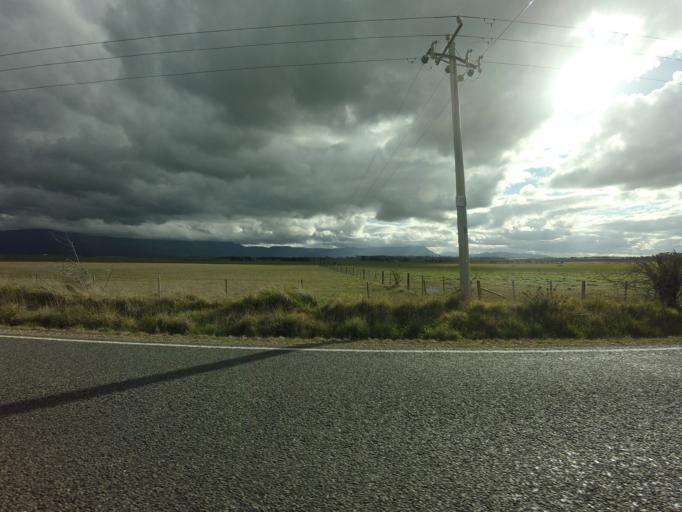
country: AU
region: Tasmania
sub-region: Northern Midlands
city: Longford
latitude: -41.7479
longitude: 147.0823
